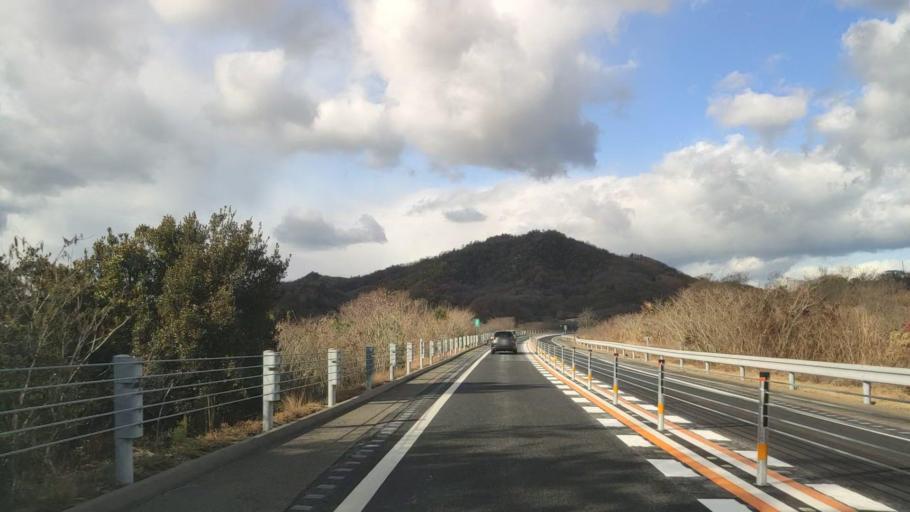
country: JP
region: Hiroshima
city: Innoshima
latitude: 34.3206
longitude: 133.1515
